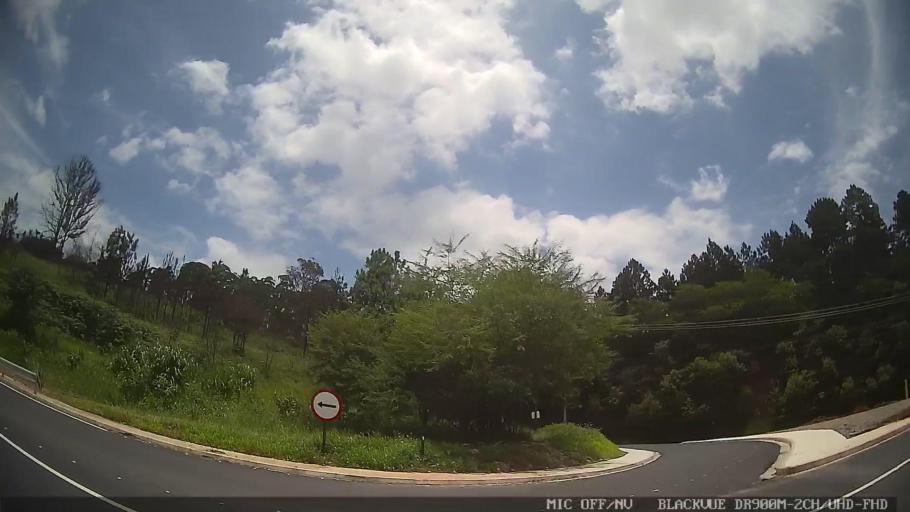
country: BR
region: Sao Paulo
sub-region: Aruja
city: Aruja
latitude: -23.4055
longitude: -46.3026
